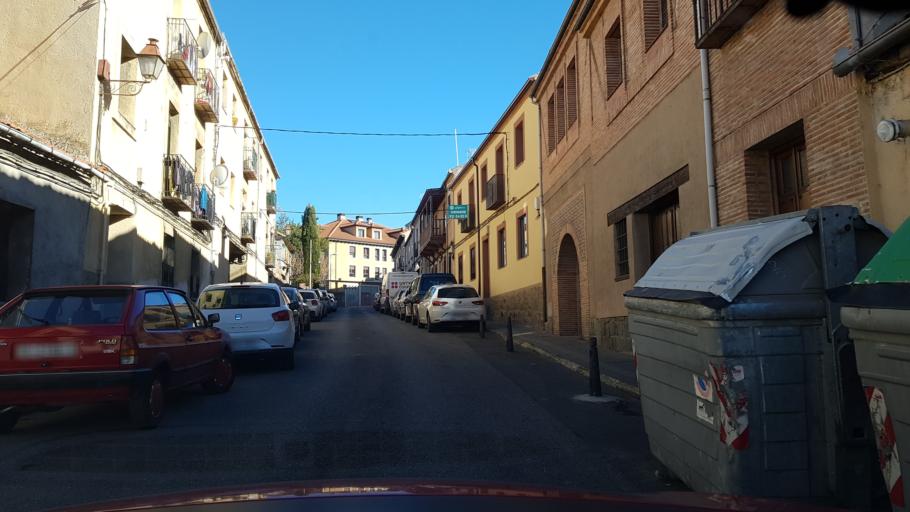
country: ES
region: Castille and Leon
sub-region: Provincia de Segovia
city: Segovia
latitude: 40.9526
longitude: -4.1132
